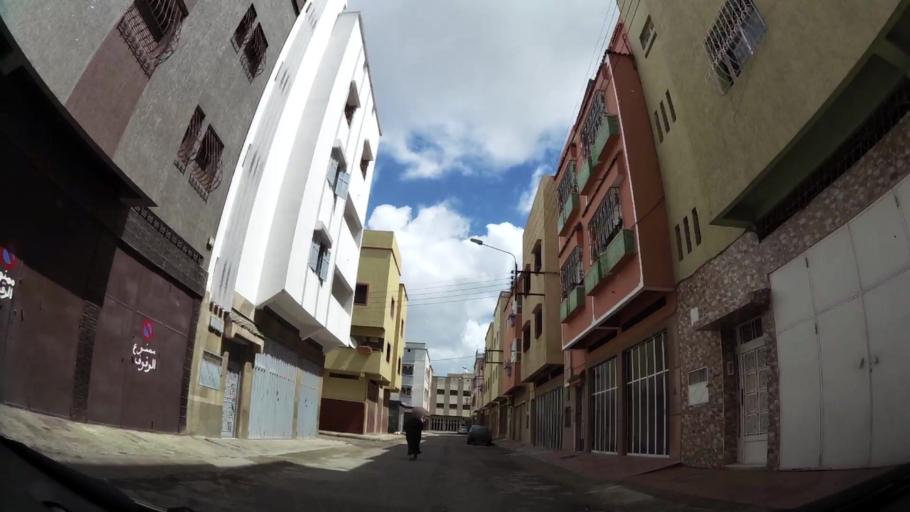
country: MA
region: Grand Casablanca
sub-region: Casablanca
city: Casablanca
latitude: 33.5417
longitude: -7.5840
